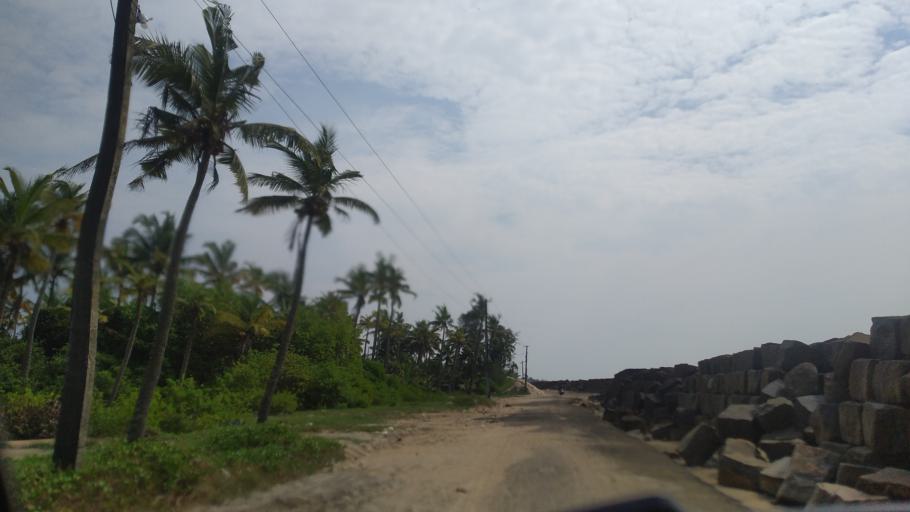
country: IN
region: Kerala
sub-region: Ernakulam
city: Elur
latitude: 10.0873
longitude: 76.1926
